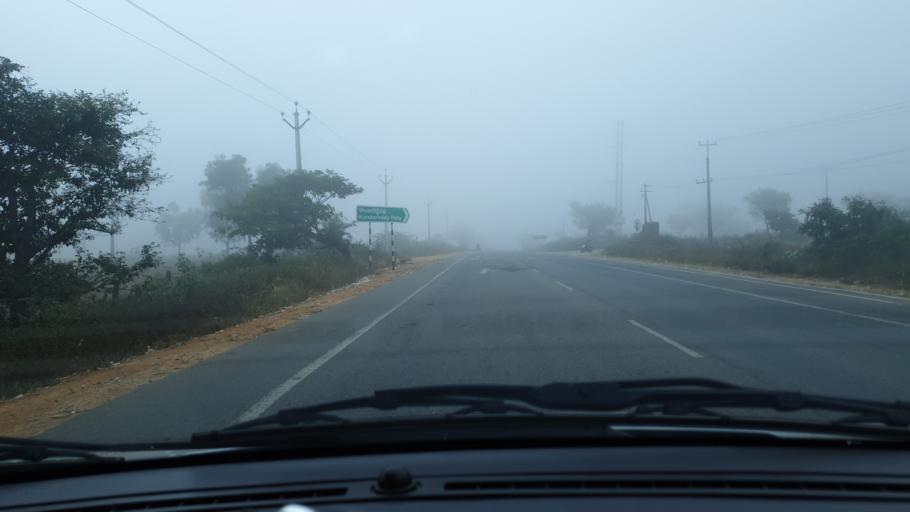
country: IN
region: Telangana
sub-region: Mahbubnagar
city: Nagar Karnul
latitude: 16.6639
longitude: 78.5644
